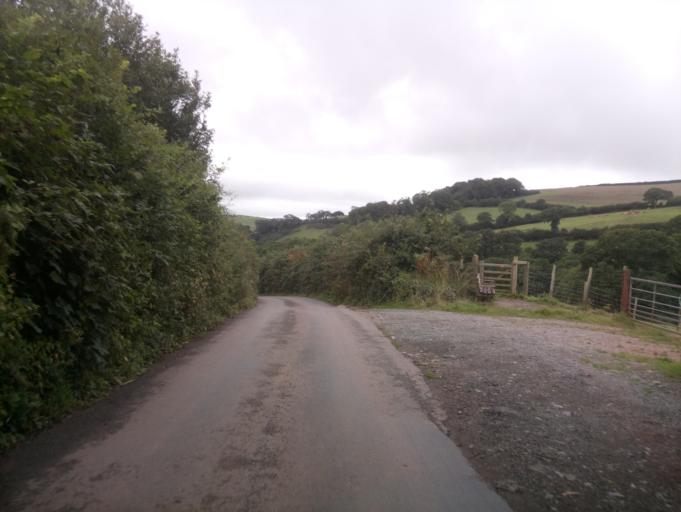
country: GB
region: England
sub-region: Devon
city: Kingsbridge
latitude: 50.2798
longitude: -3.7196
